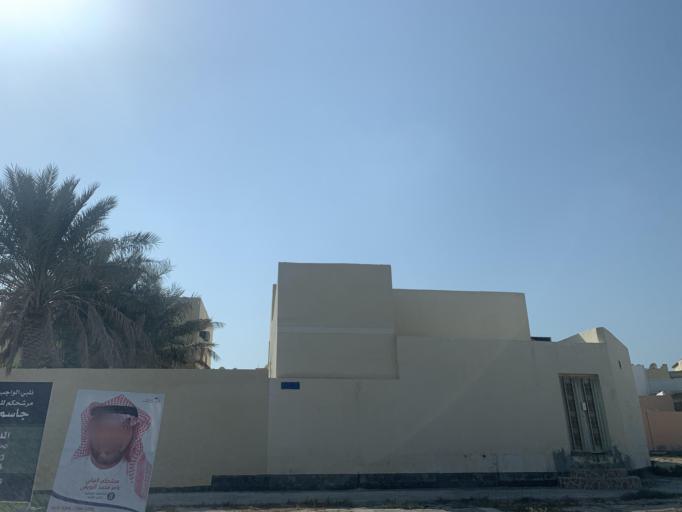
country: BH
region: Central Governorate
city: Madinat Hamad
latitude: 26.1385
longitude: 50.5053
